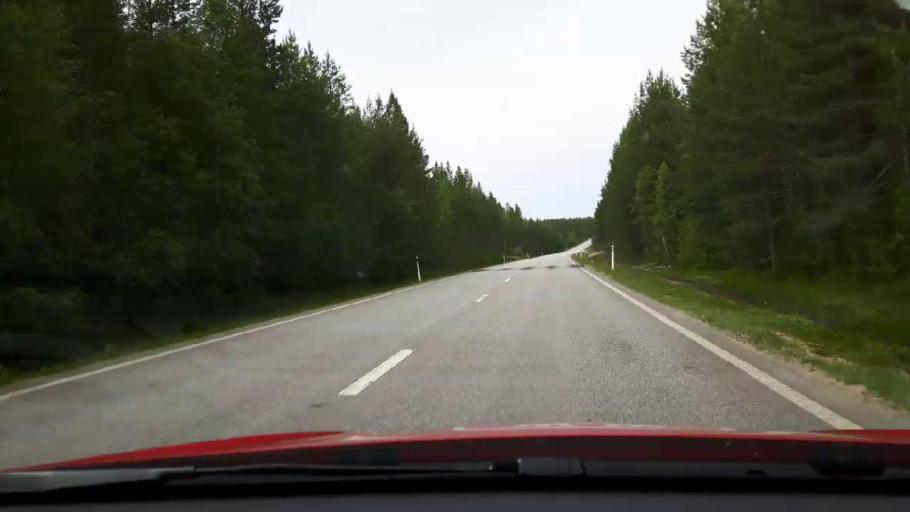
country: SE
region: Jaemtland
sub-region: Harjedalens Kommun
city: Sveg
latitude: 62.1090
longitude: 14.1918
